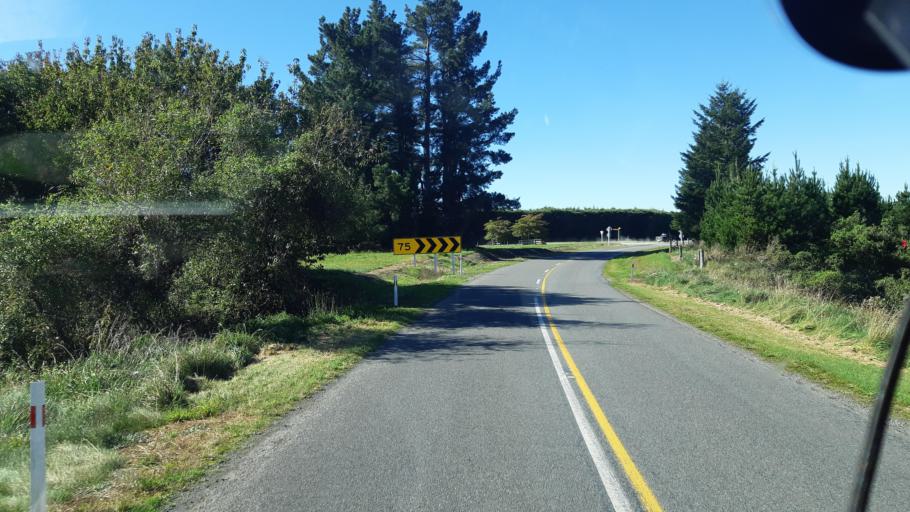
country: NZ
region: Canterbury
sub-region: Waimakariri District
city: Oxford
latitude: -43.2256
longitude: 172.3484
